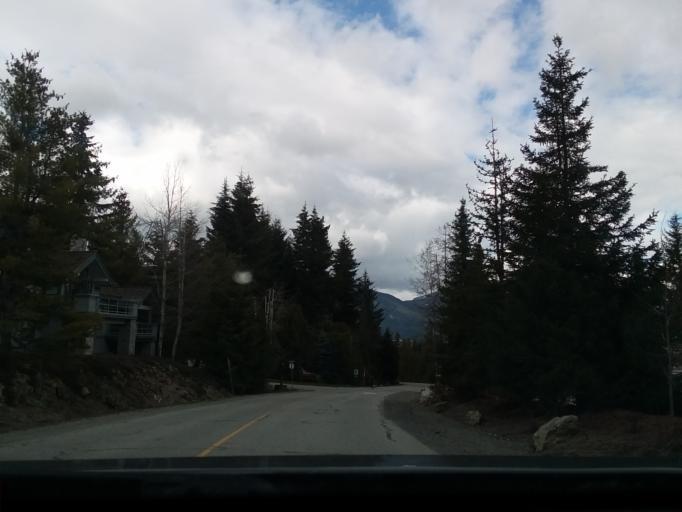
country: CA
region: British Columbia
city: Whistler
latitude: 50.1177
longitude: -122.9694
